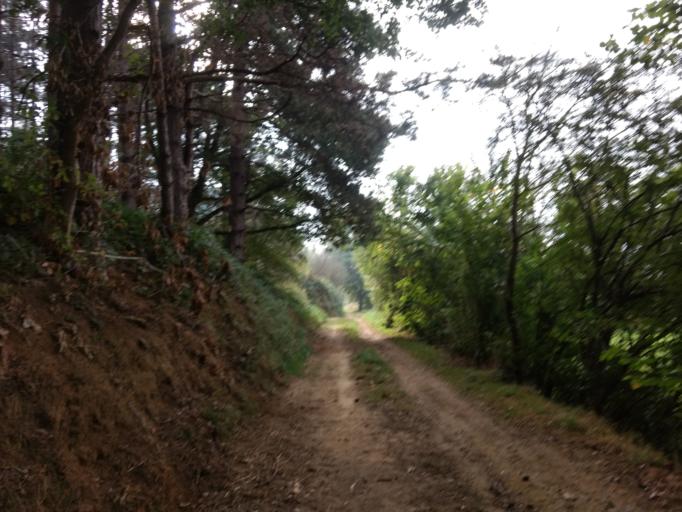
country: BE
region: Flanders
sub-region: Provincie Vlaams-Brabant
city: Bertem
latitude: 50.8726
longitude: 4.6419
